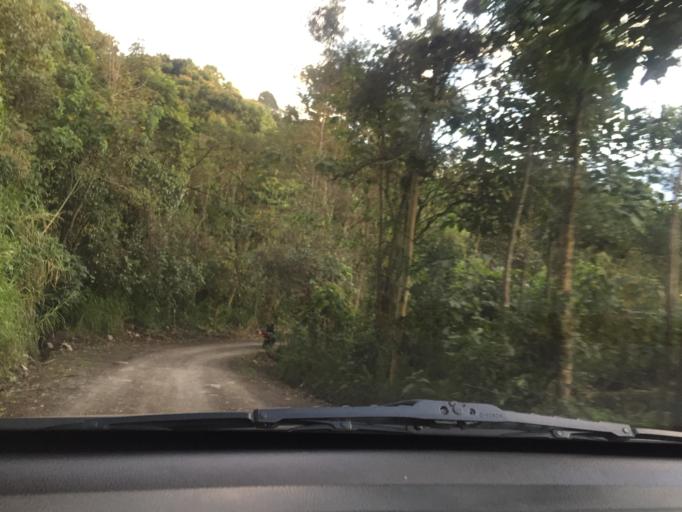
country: CO
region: Cundinamarca
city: Zipacon
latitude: 4.7065
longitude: -74.4053
